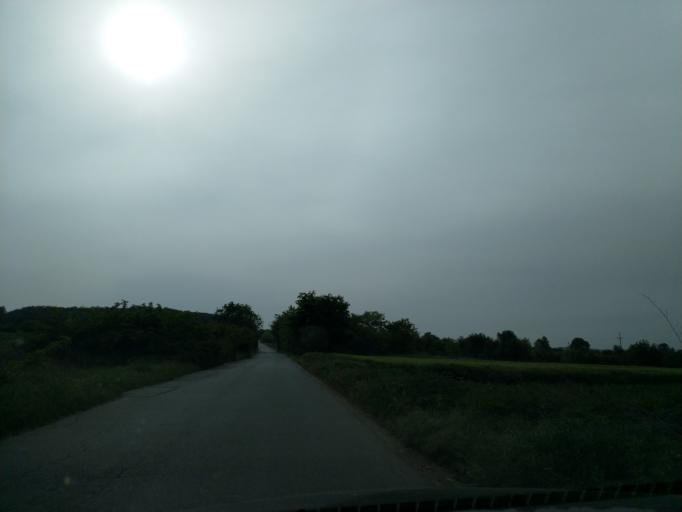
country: RS
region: Central Serbia
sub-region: Pomoravski Okrug
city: Jagodina
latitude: 43.9732
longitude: 21.2154
